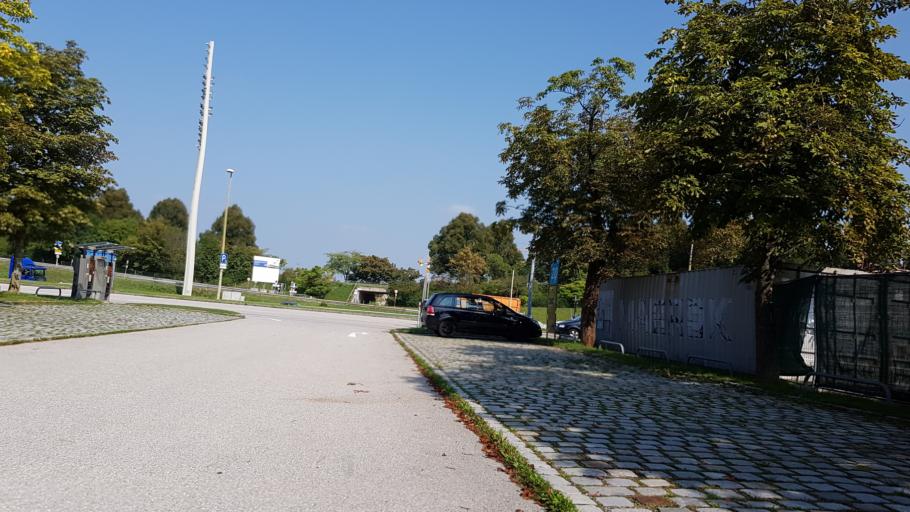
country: DE
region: Bavaria
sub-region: Upper Bavaria
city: Munich
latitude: 48.1754
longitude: 11.5448
